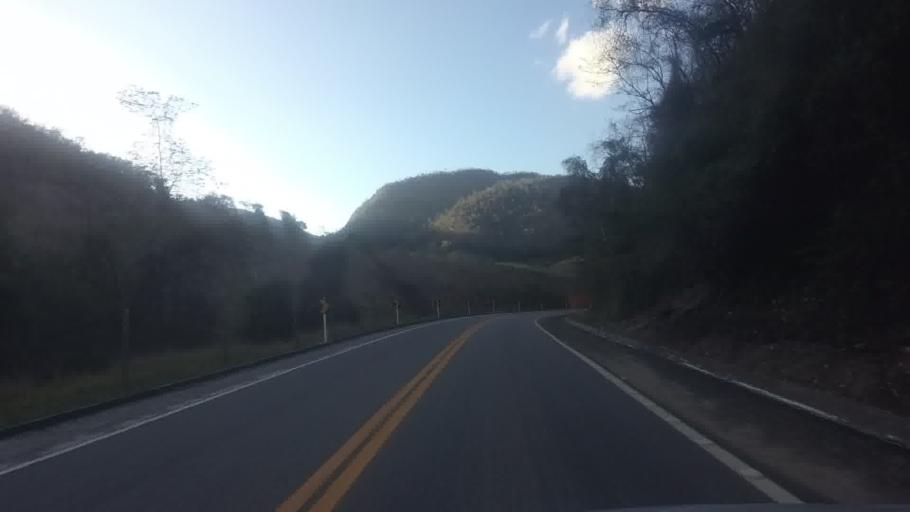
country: BR
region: Espirito Santo
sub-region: Cachoeiro De Itapemirim
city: Cachoeiro de Itapemirim
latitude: -20.8269
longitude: -41.2191
